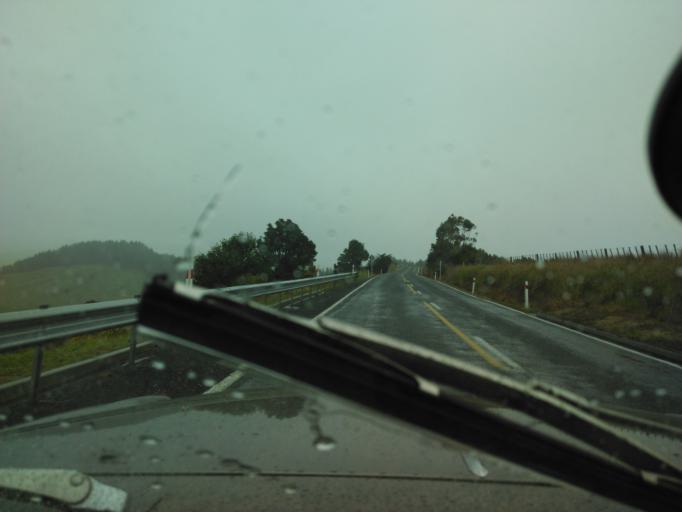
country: NZ
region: Auckland
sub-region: Auckland
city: Wellsford
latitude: -36.3558
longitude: 174.4702
